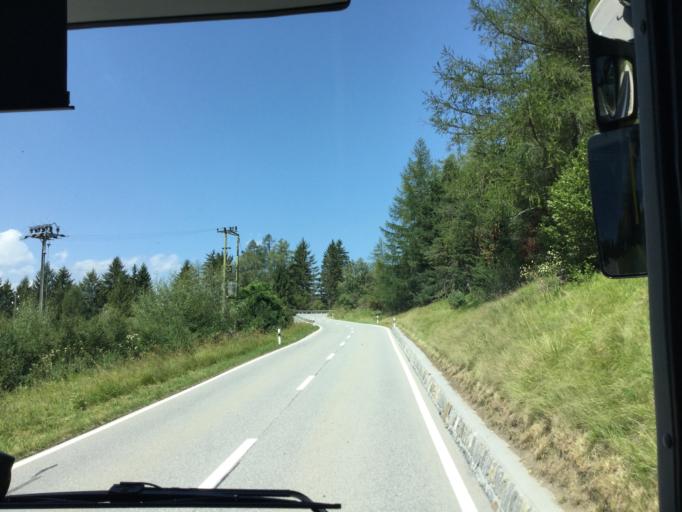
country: CH
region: Grisons
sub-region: Albula District
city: Tiefencastel
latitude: 46.6716
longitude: 9.5753
